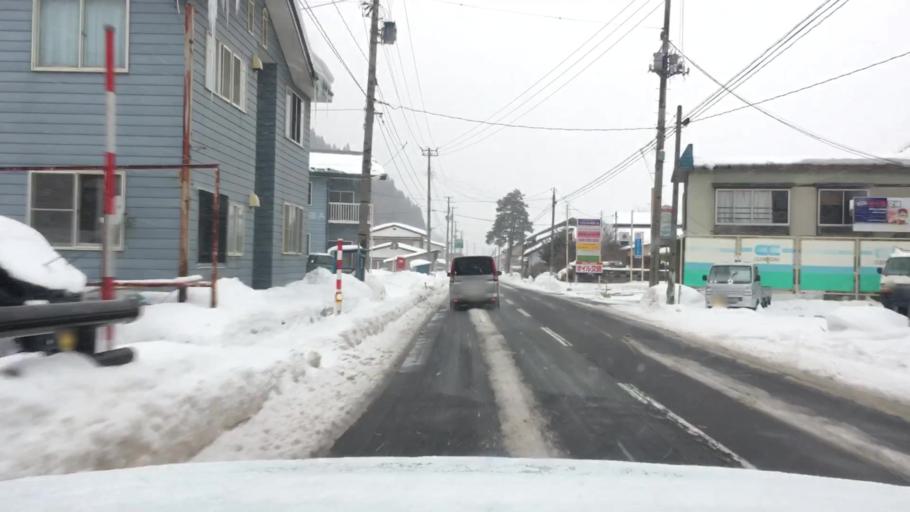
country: JP
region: Iwate
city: Ichinohe
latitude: 40.0919
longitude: 141.0469
